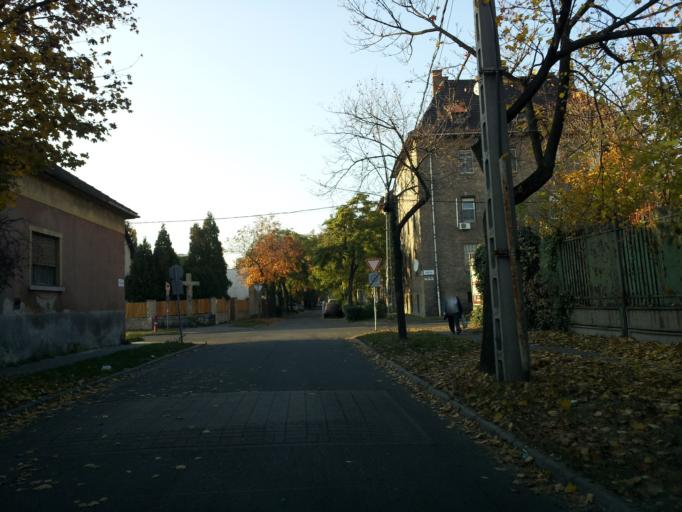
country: HU
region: Budapest
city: Budapest X. keruelet
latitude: 47.4807
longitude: 19.1563
